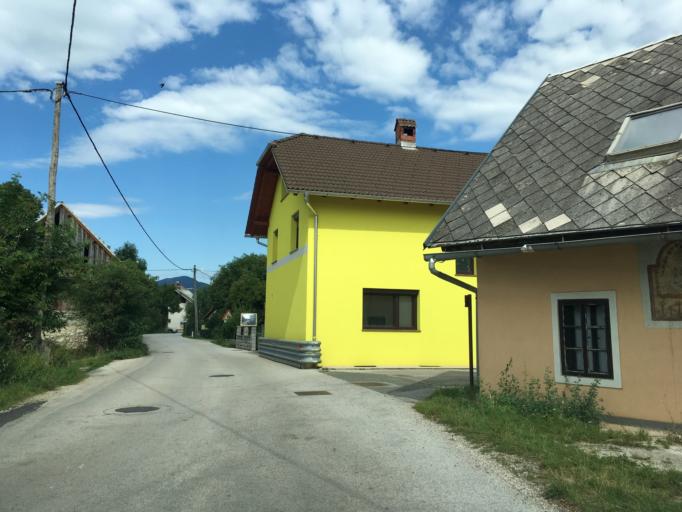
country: SI
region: Radovljica
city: Lesce
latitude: 46.3883
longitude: 14.1679
